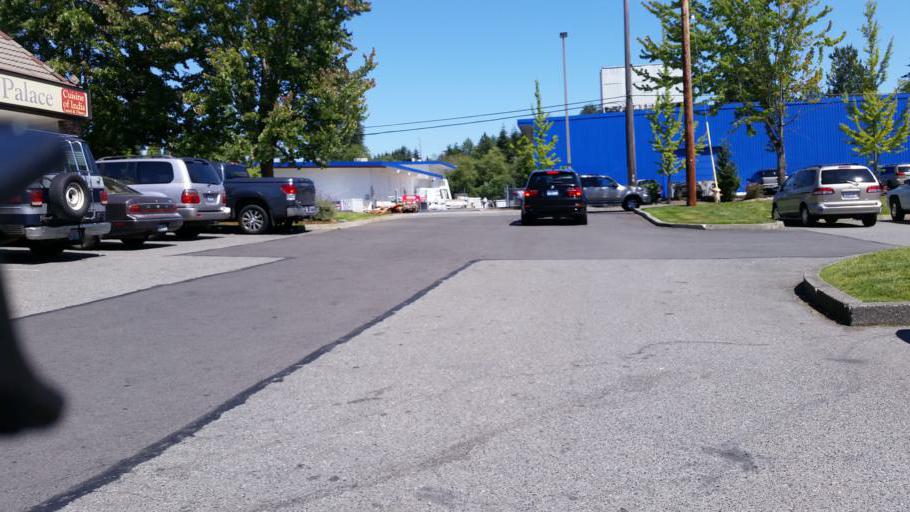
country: US
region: Washington
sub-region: King County
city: Bellevue
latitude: 47.6308
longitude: -122.1543
